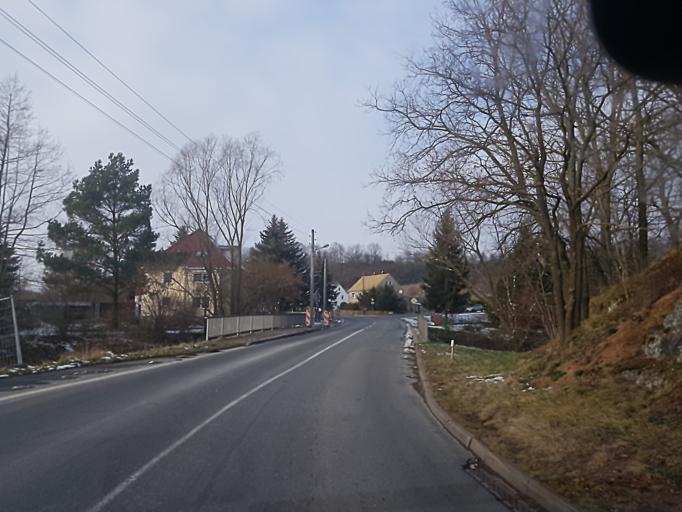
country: DE
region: Saxony
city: Leisnig
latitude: 51.1744
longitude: 12.9152
